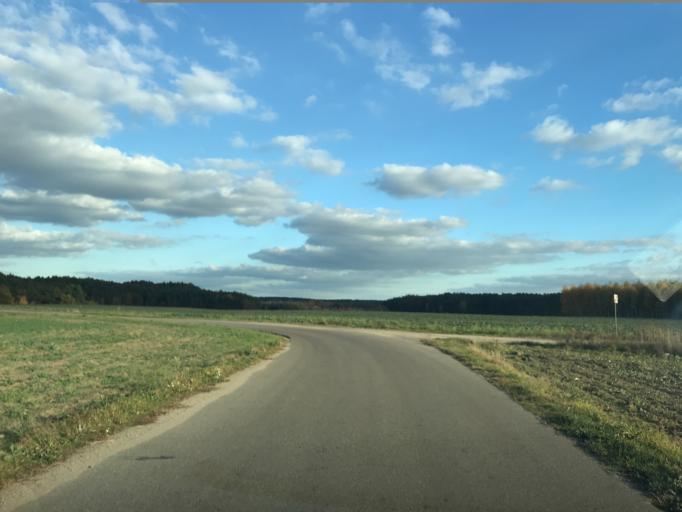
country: PL
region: Warmian-Masurian Voivodeship
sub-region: Powiat dzialdowski
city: Rybno
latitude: 53.3740
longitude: 19.8346
